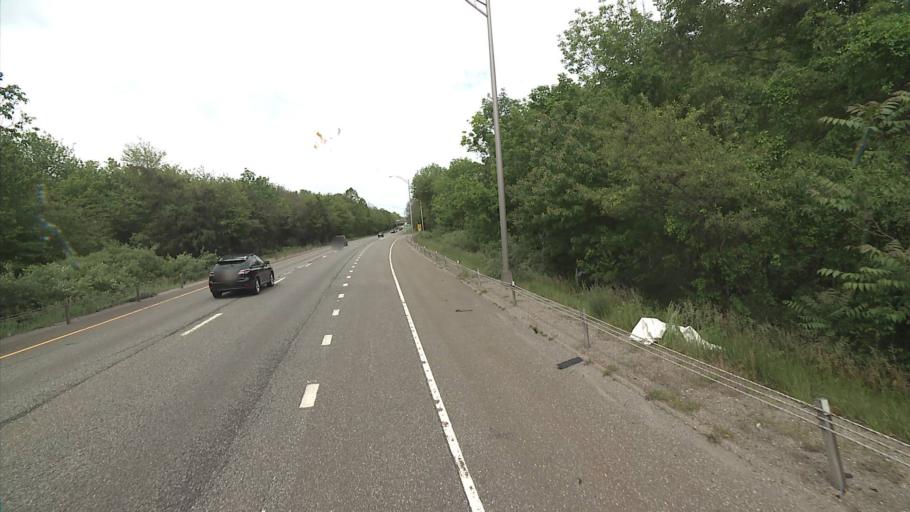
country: US
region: Connecticut
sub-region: New London County
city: Mystic
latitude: 41.3713
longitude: -71.9757
